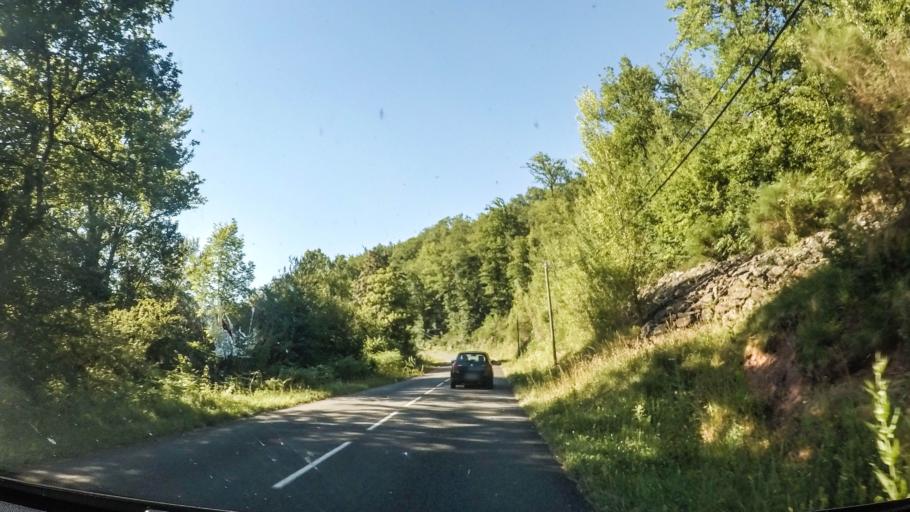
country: FR
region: Midi-Pyrenees
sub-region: Departement de l'Aveyron
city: Saint-Christophe-Vallon
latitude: 44.5523
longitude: 2.3966
